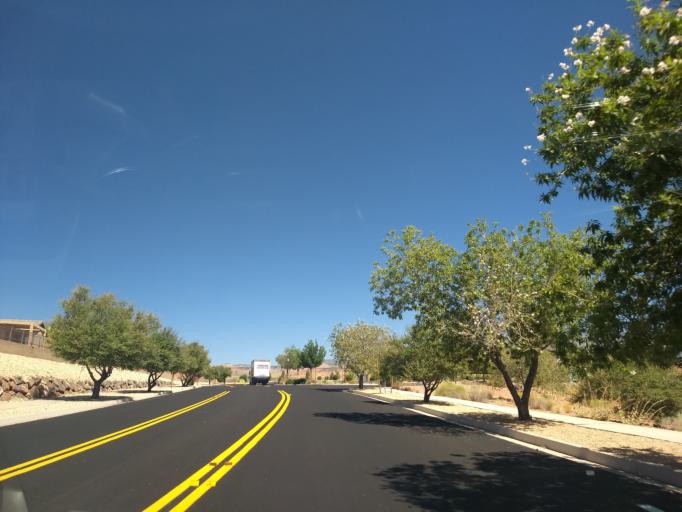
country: US
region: Utah
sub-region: Washington County
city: Washington
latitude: 37.1470
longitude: -113.4644
